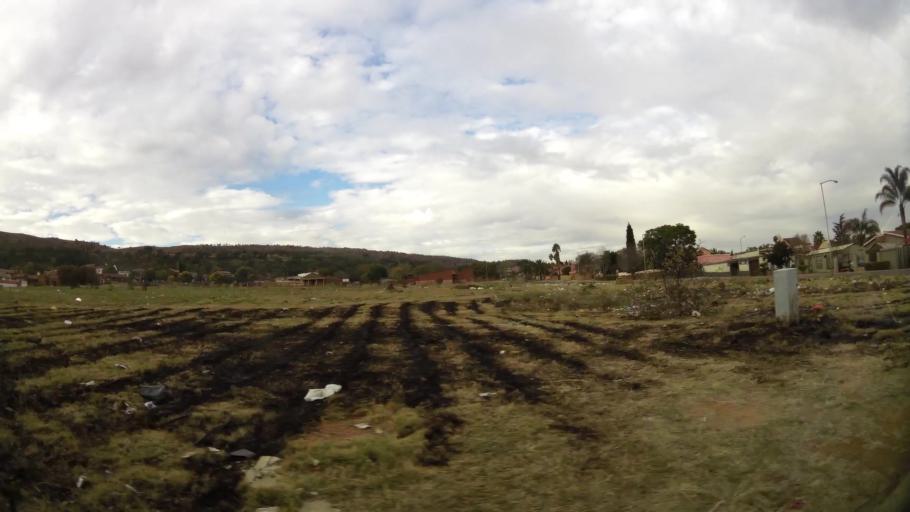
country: ZA
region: Gauteng
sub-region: City of Tshwane Metropolitan Municipality
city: Pretoria
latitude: -25.6995
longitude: 28.3047
